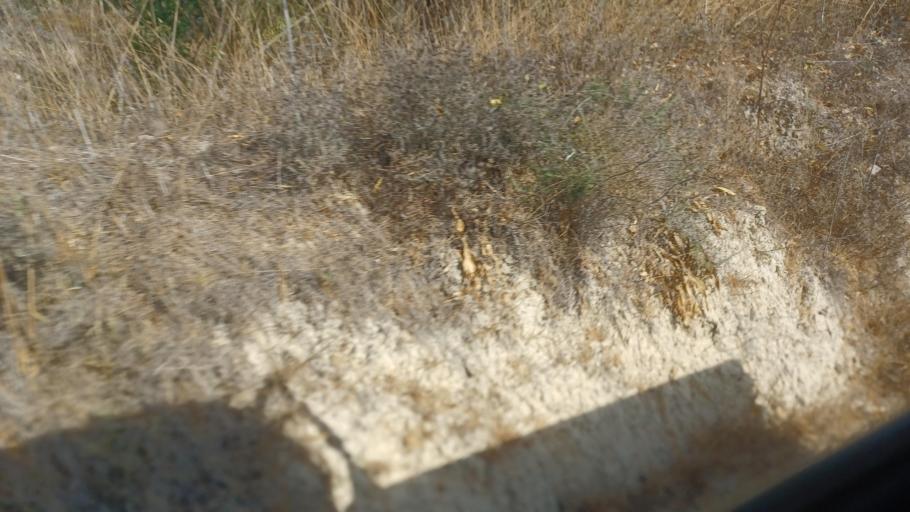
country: CY
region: Pafos
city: Mesogi
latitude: 34.8551
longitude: 32.4742
